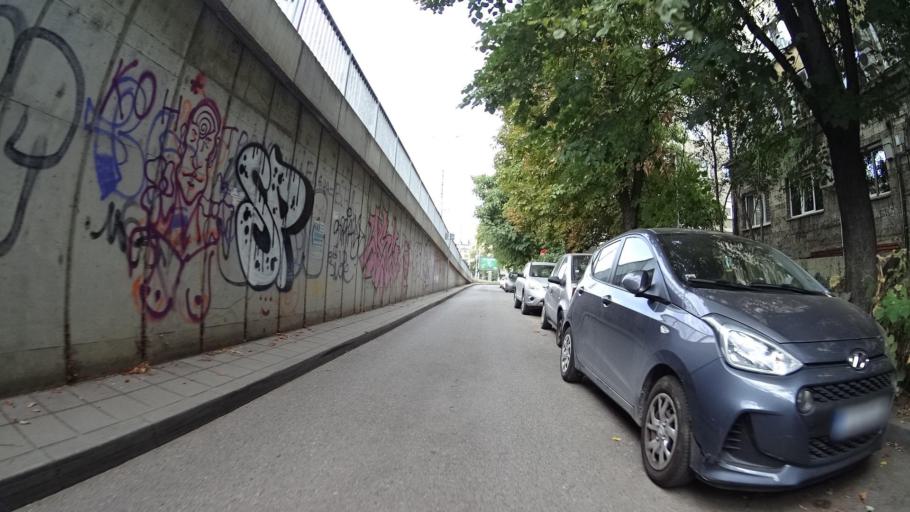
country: BG
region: Plovdiv
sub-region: Obshtina Plovdiv
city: Plovdiv
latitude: 42.1549
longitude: 24.7390
